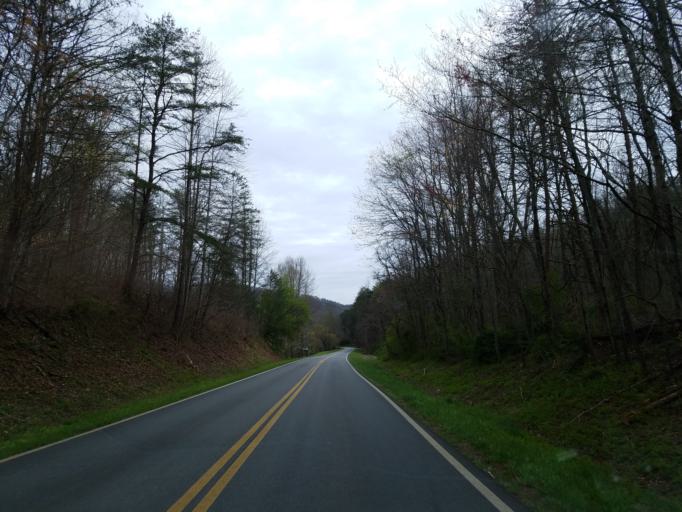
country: US
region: Georgia
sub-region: Fannin County
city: Blue Ridge
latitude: 34.8397
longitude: -84.2977
